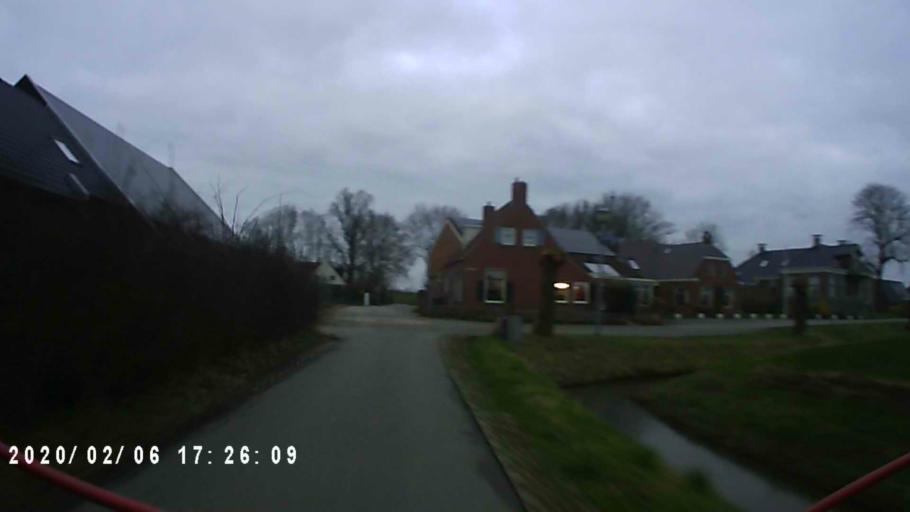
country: NL
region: Groningen
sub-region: Gemeente Winsum
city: Winsum
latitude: 53.3003
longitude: 6.5303
